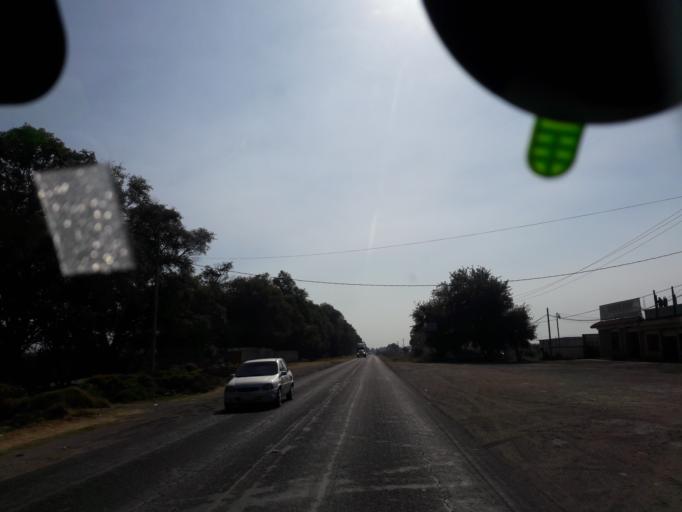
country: MX
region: Tlaxcala
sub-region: Ixtacuixtla de Mariano Matamoros
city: Santa Justina Ecatepec
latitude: 19.3080
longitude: -98.3675
